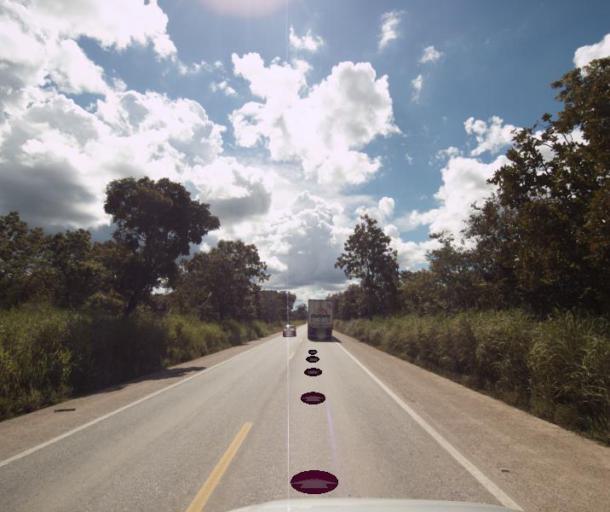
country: BR
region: Goias
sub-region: Porangatu
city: Porangatu
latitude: -13.5649
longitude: -49.0540
